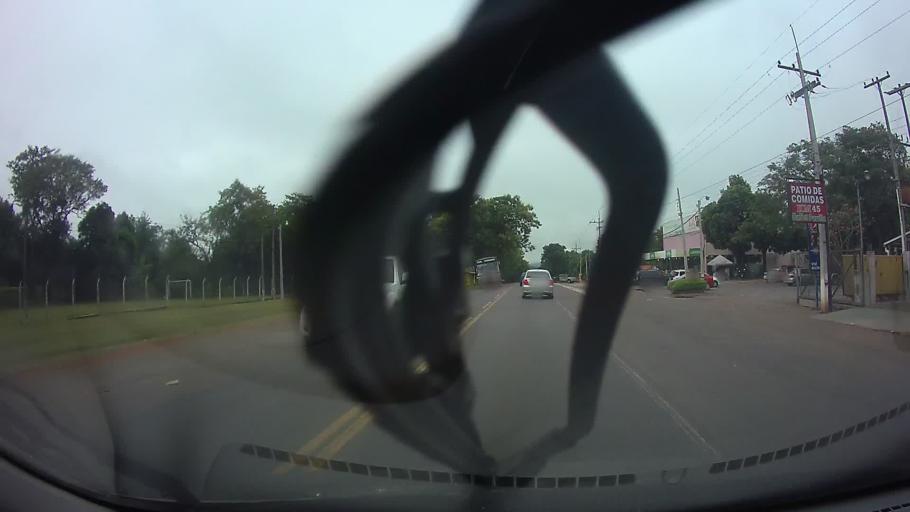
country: PY
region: Paraguari
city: Yaguaron
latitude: -25.5473
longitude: -57.3075
